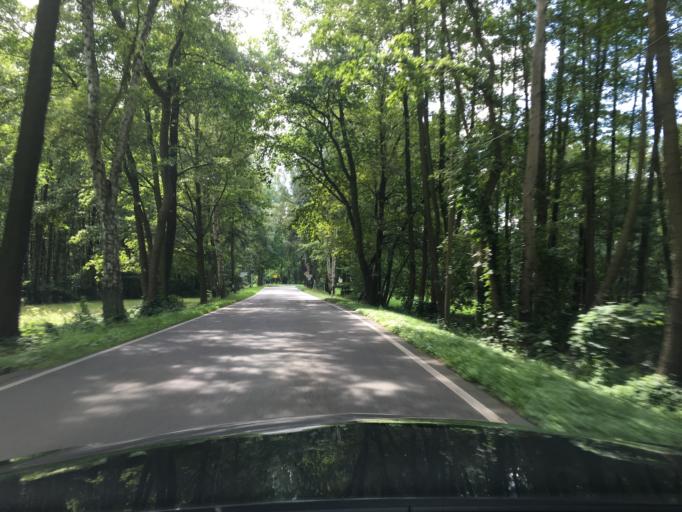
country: DE
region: Brandenburg
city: Burg
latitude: 51.8285
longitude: 14.1038
